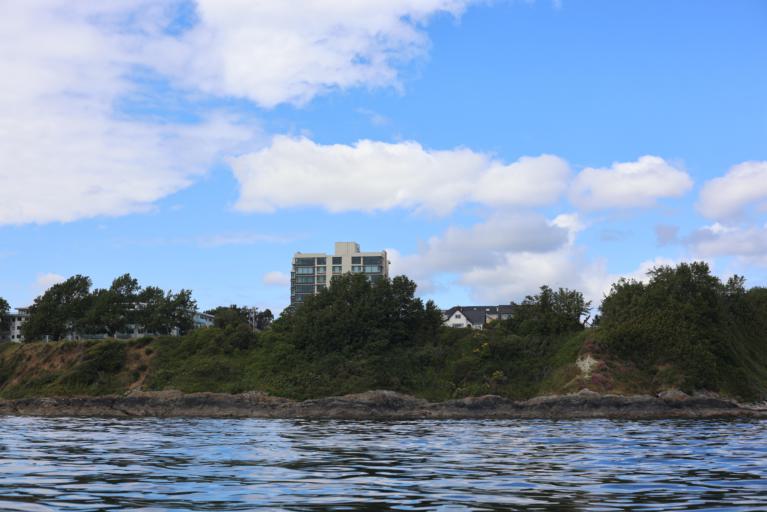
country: CA
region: British Columbia
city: Victoria
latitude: 48.4062
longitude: -123.3705
